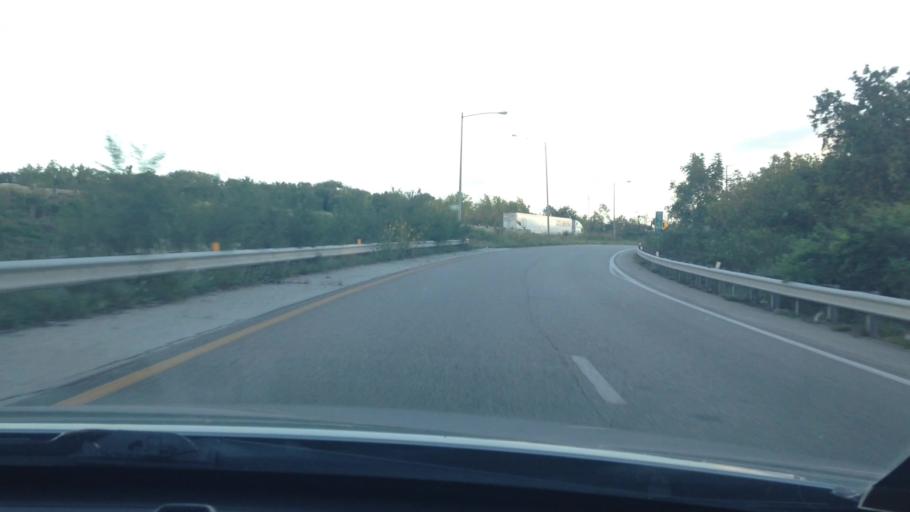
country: US
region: Missouri
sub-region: Jackson County
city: Raytown
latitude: 39.0584
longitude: -94.4925
